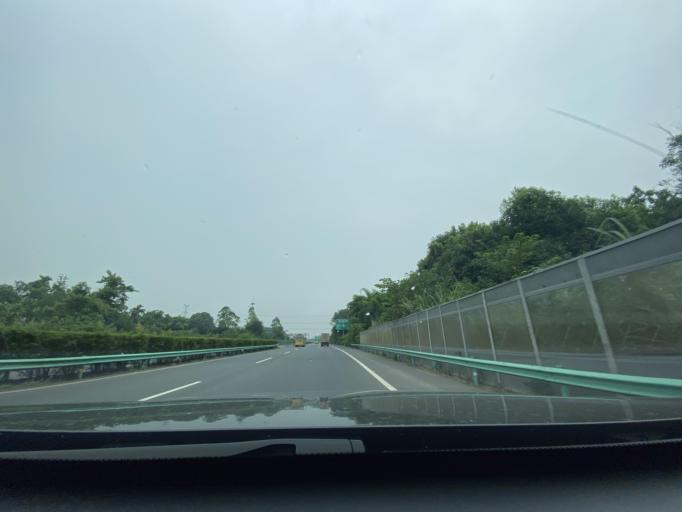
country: CN
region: Sichuan
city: Longquan
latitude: 30.3308
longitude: 104.1200
